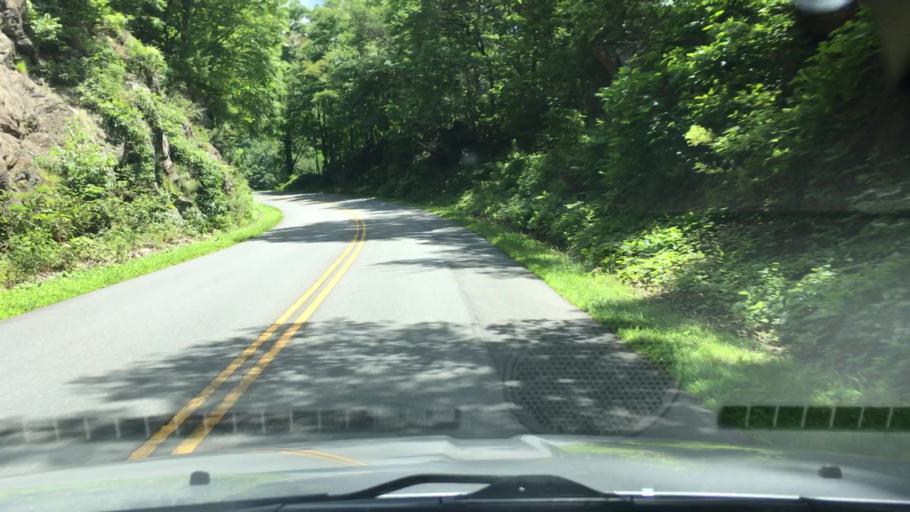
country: US
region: North Carolina
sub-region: Buncombe County
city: Swannanoa
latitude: 35.6605
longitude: -82.4586
